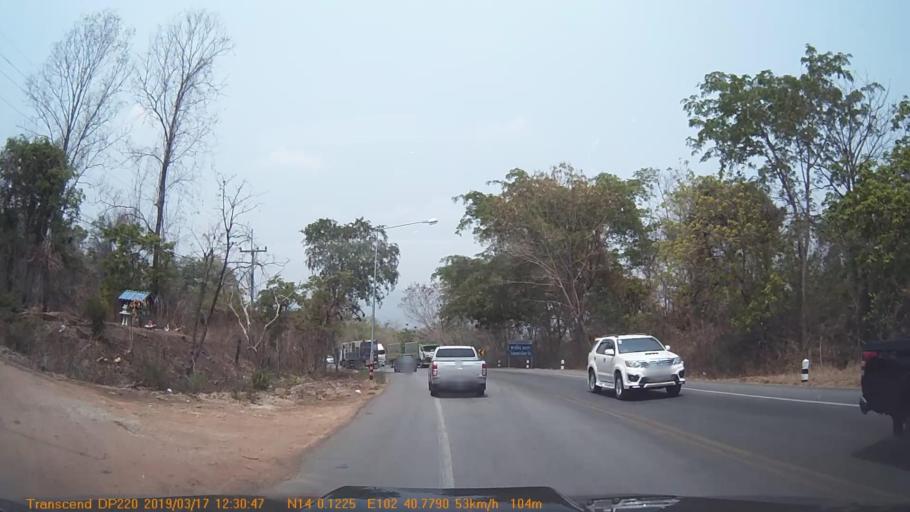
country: TH
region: Sa Kaeo
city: Ta Phraya
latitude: 14.0022
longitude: 102.6796
